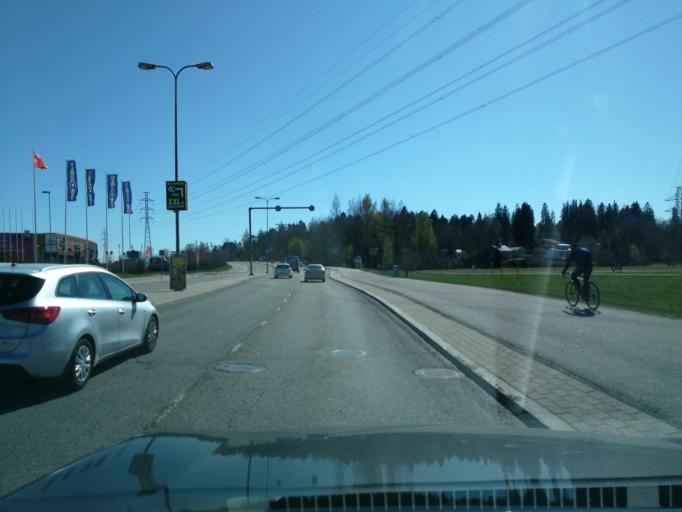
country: FI
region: Uusimaa
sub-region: Helsinki
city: Vantaa
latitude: 60.2802
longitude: 24.9716
